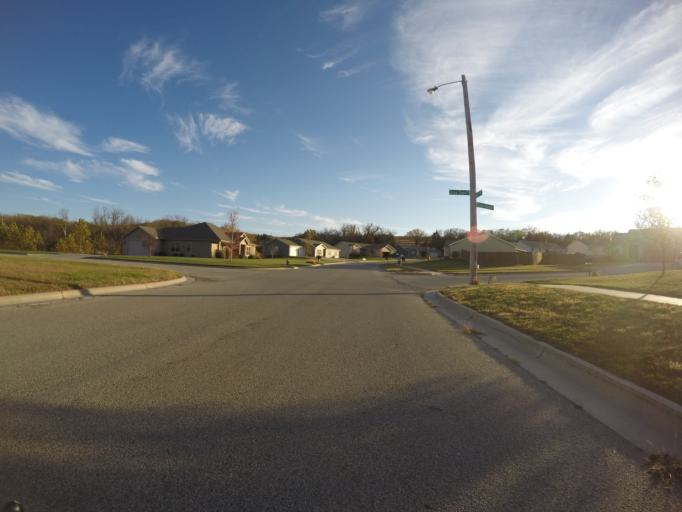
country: US
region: Kansas
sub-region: Riley County
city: Manhattan
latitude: 39.1835
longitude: -96.6381
